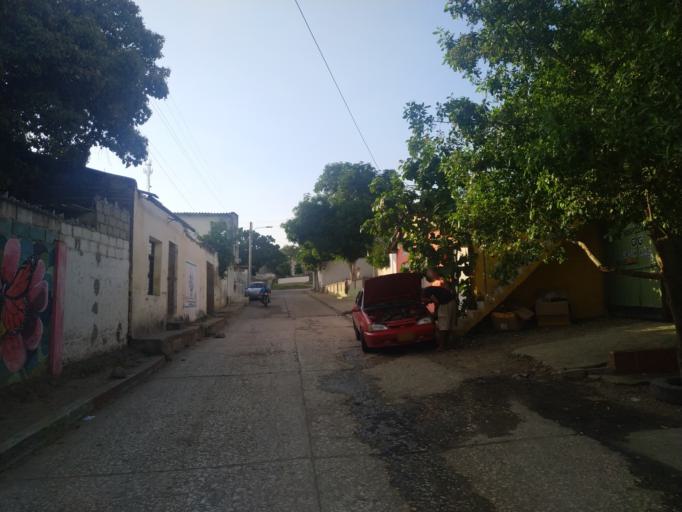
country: CO
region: Bolivar
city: San Estanislao
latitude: 10.3966
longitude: -75.1475
